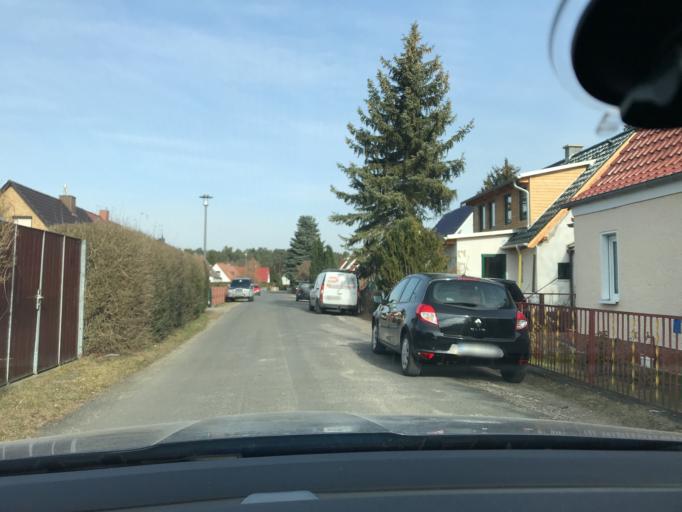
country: DE
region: Brandenburg
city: Erkner
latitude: 52.4080
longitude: 13.7648
